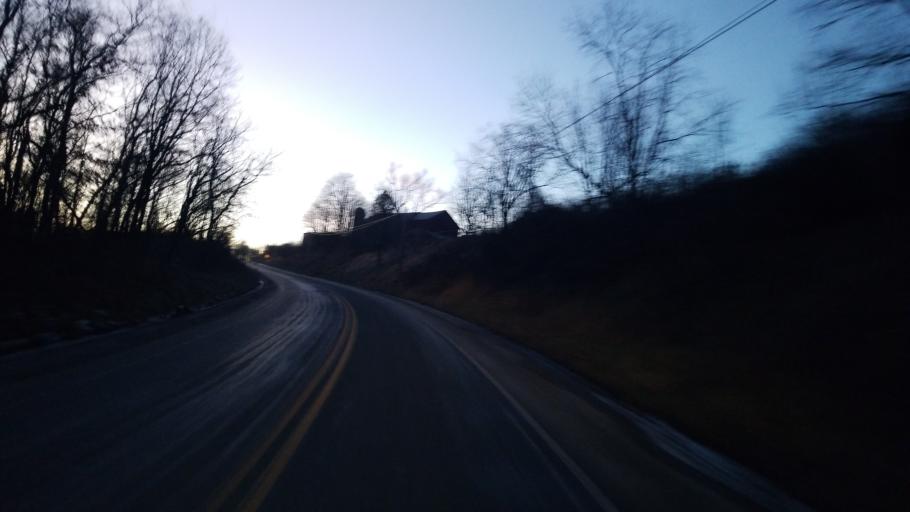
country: US
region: Pennsylvania
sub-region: Jefferson County
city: Punxsutawney
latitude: 40.8691
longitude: -79.1820
